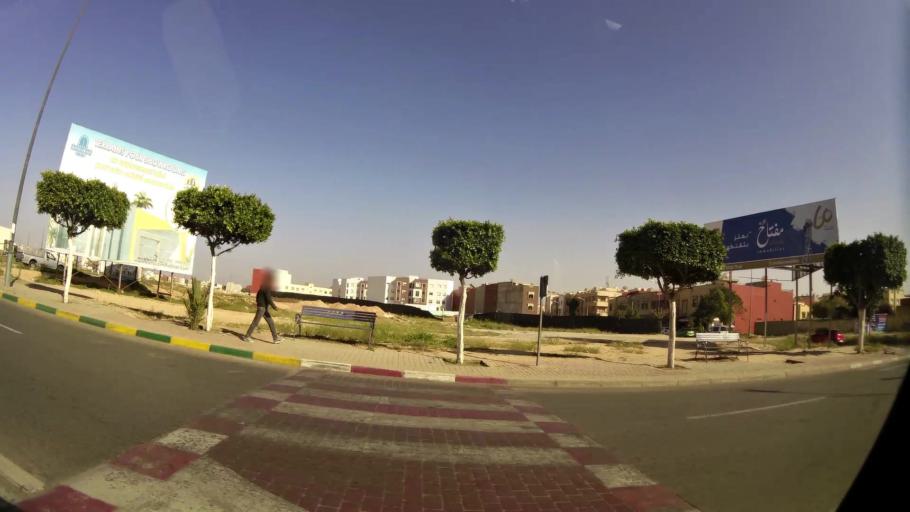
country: MA
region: Souss-Massa-Draa
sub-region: Inezgane-Ait Mellou
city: Inezgane
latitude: 30.3780
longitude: -9.5257
